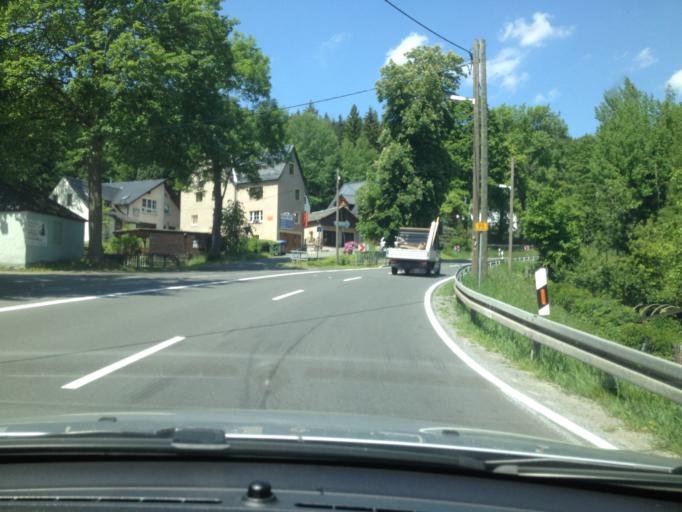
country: DE
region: Saxony
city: Ehrenfriedersdorf
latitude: 50.6622
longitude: 12.9654
